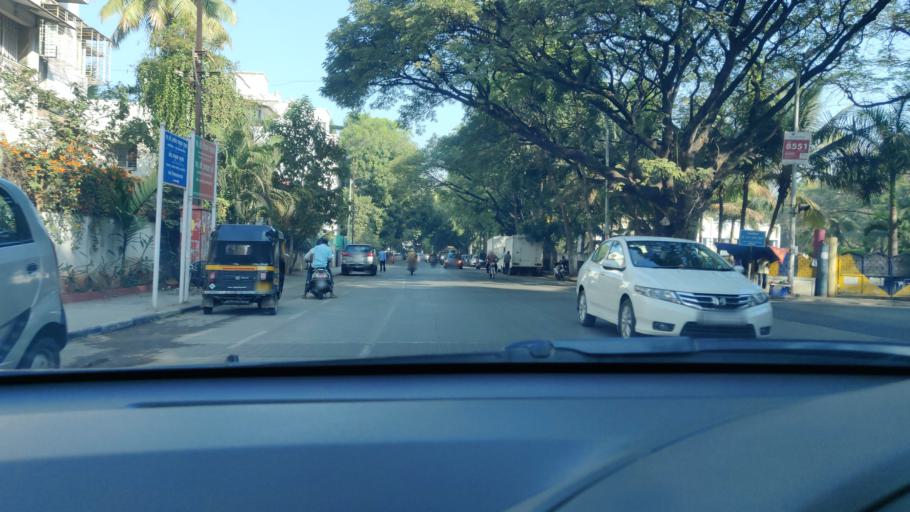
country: IN
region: Maharashtra
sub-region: Pune Division
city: Khadki
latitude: 18.5559
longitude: 73.8046
